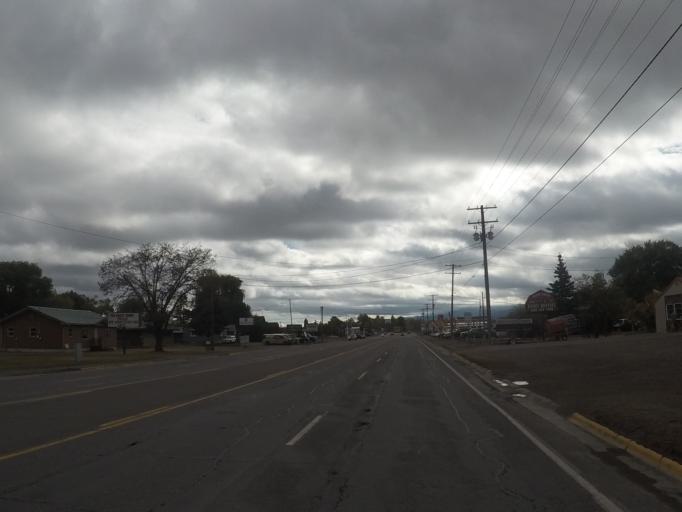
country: US
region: Montana
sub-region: Flathead County
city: Evergreen
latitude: 48.2208
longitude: -114.2774
